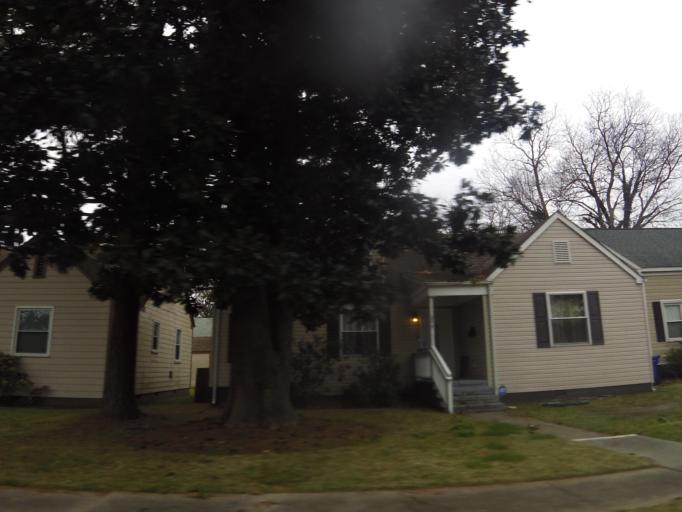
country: US
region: Virginia
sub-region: City of Portsmouth
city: Portsmouth
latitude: 36.8402
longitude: -76.3268
